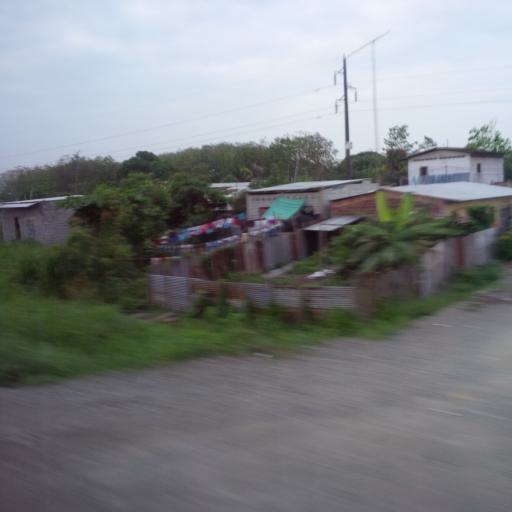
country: EC
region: Canar
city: La Troncal
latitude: -2.3413
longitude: -79.3799
